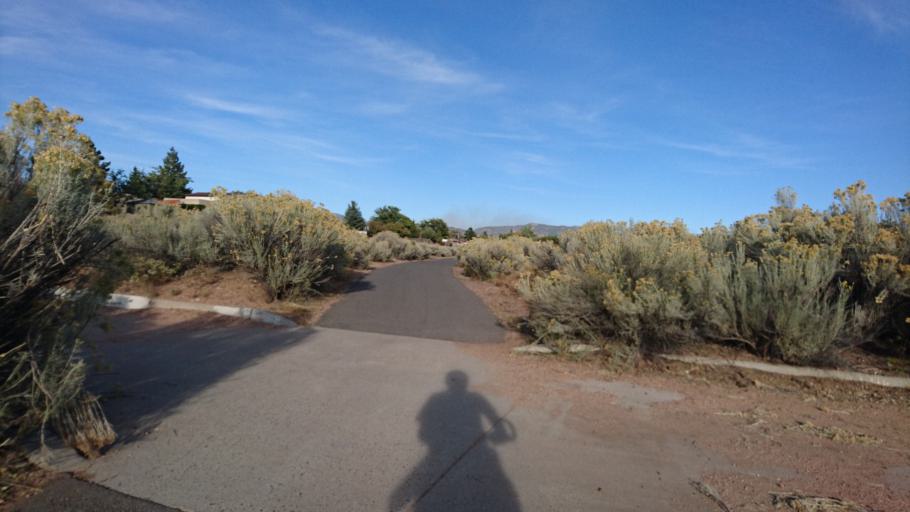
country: US
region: New Mexico
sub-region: Santa Fe County
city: Agua Fria
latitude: 35.6419
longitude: -105.9869
